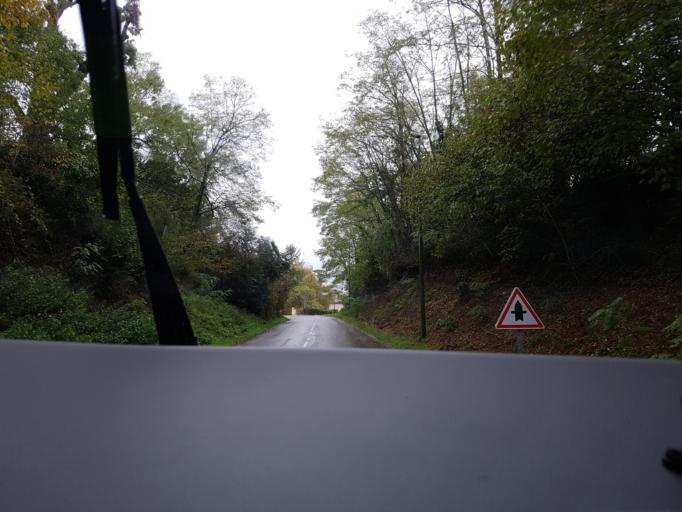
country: FR
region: Aquitaine
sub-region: Departement de la Gironde
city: Saint-Symphorien
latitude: 44.3299
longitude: -0.5872
